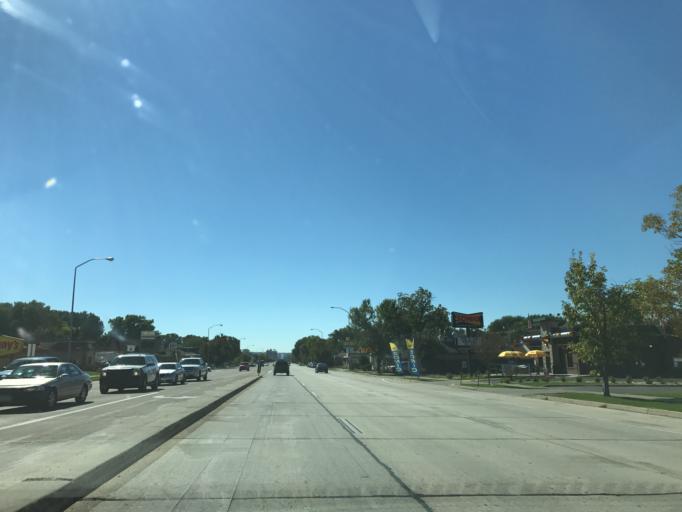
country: US
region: Utah
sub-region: Weber County
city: Ogden
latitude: 41.2439
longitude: -111.9700
